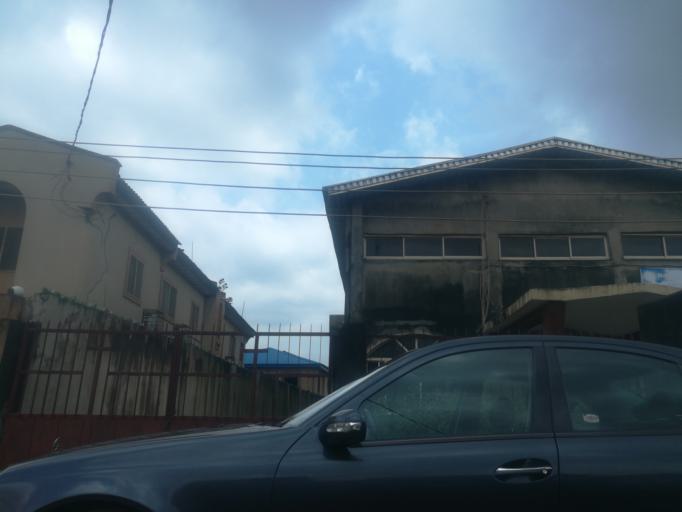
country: NG
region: Lagos
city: Somolu
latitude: 6.5575
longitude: 3.3943
